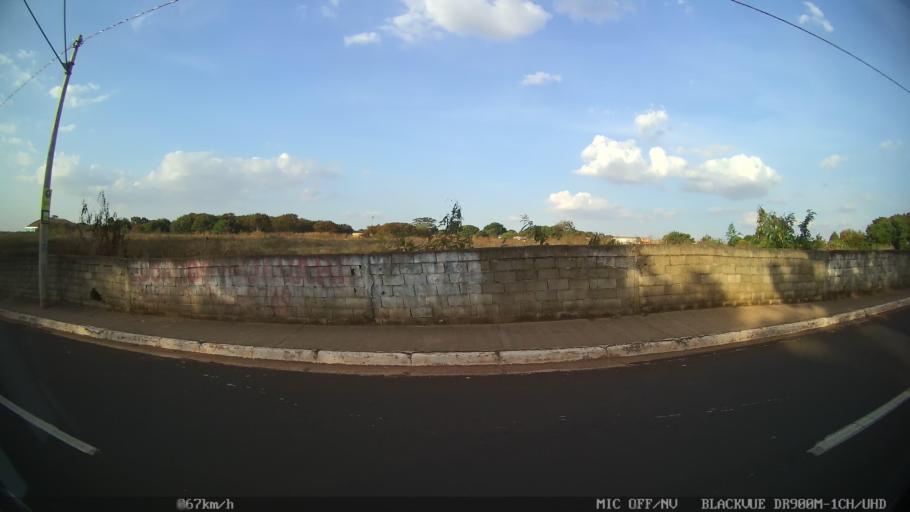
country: BR
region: Sao Paulo
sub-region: Ribeirao Preto
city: Ribeirao Preto
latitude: -21.1357
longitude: -47.8033
